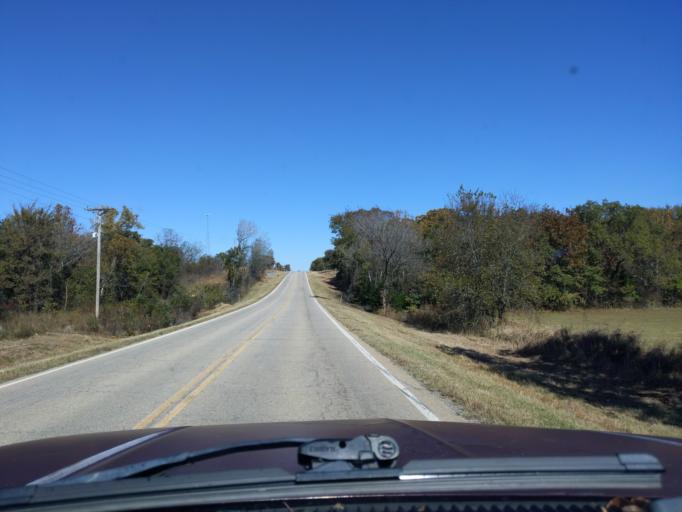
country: US
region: Oklahoma
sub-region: Creek County
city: Bristow
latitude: 35.7122
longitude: -96.3872
